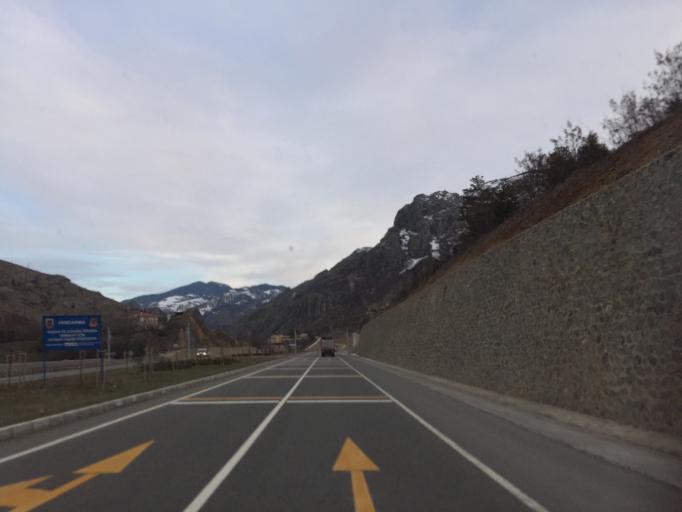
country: TR
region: Gumushane
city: Gumushkhane
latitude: 40.5040
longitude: 39.4258
